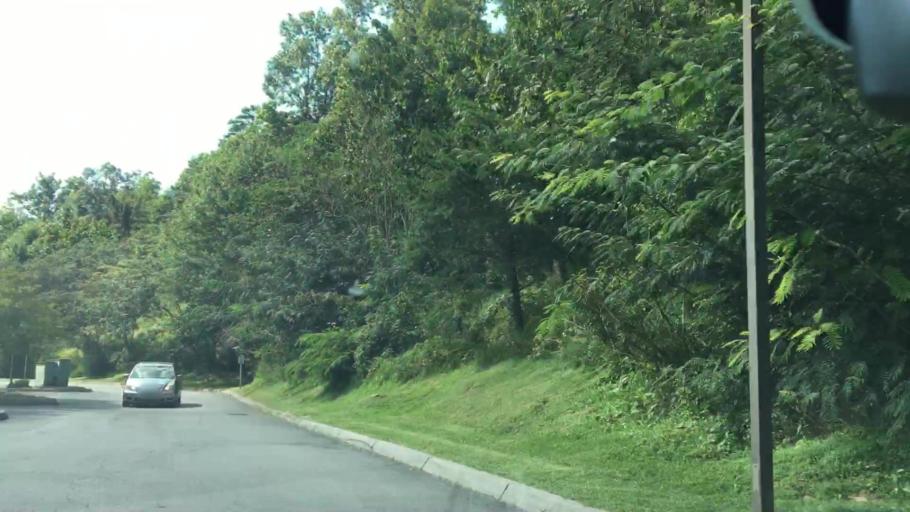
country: US
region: Tennessee
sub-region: Sevier County
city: Gatlinburg
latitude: 35.7309
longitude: -83.4818
